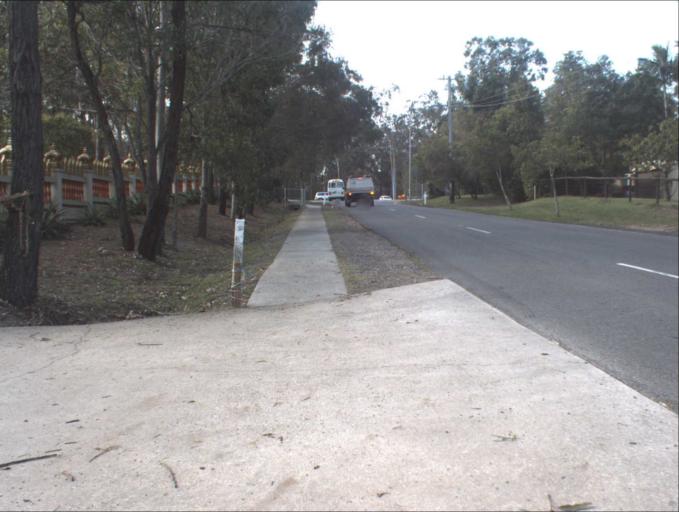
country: AU
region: Queensland
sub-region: Brisbane
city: Forest Lake
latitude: -27.6567
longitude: 153.0033
